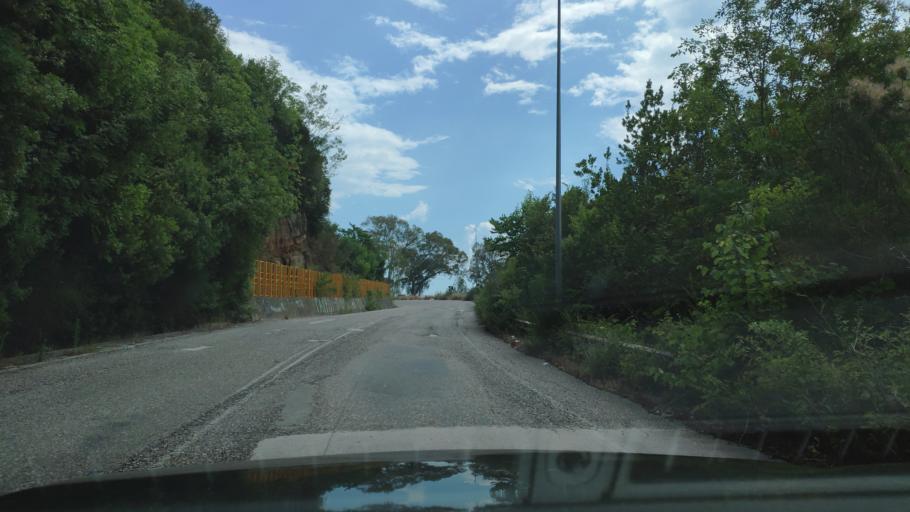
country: GR
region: West Greece
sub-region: Nomos Aitolias kai Akarnanias
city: Menidi
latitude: 39.0217
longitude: 21.1349
